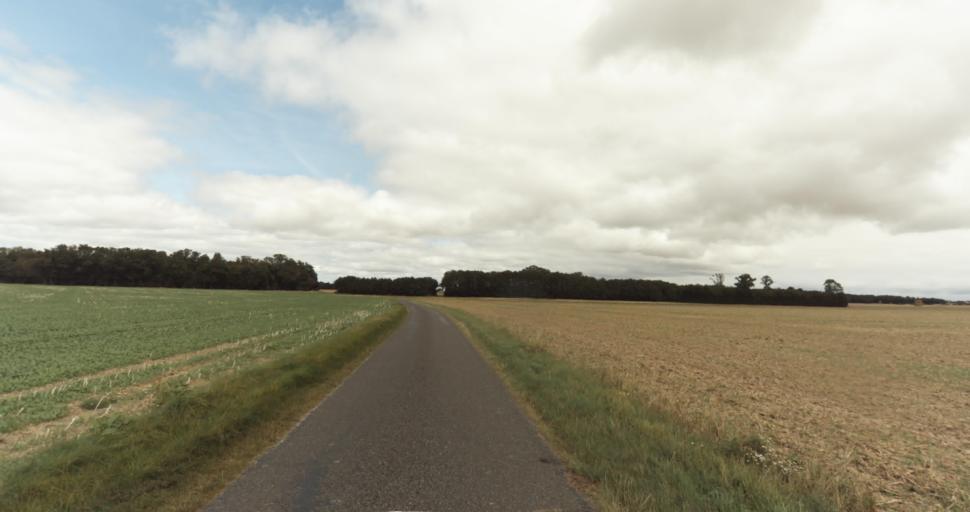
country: FR
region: Haute-Normandie
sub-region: Departement de l'Eure
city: La Madeleine-de-Nonancourt
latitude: 48.8968
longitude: 1.1996
